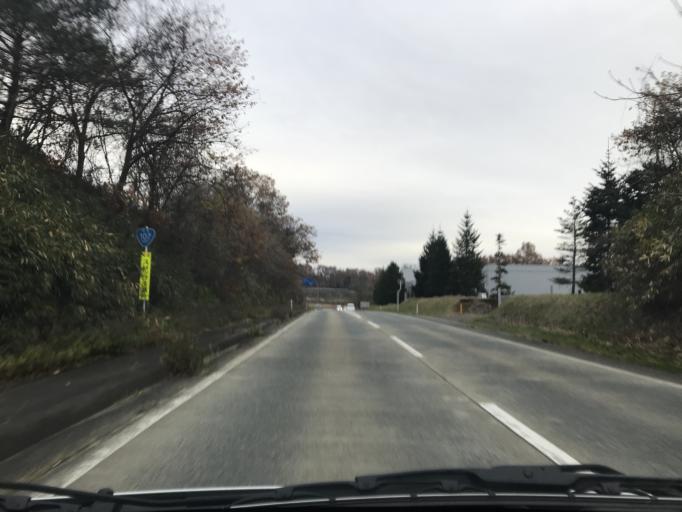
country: JP
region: Iwate
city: Kitakami
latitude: 39.2889
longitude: 141.2167
